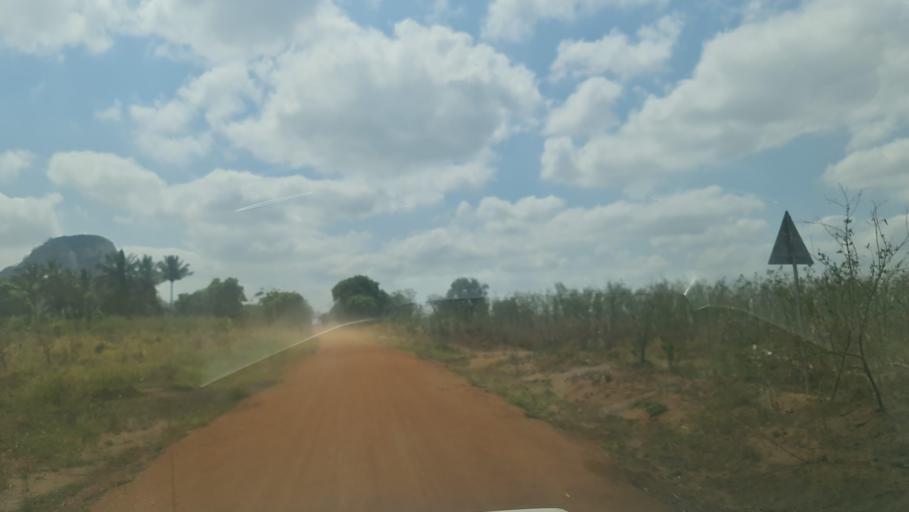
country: MW
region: Southern Region
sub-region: Nsanje District
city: Nsanje
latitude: -17.3954
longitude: 35.5670
